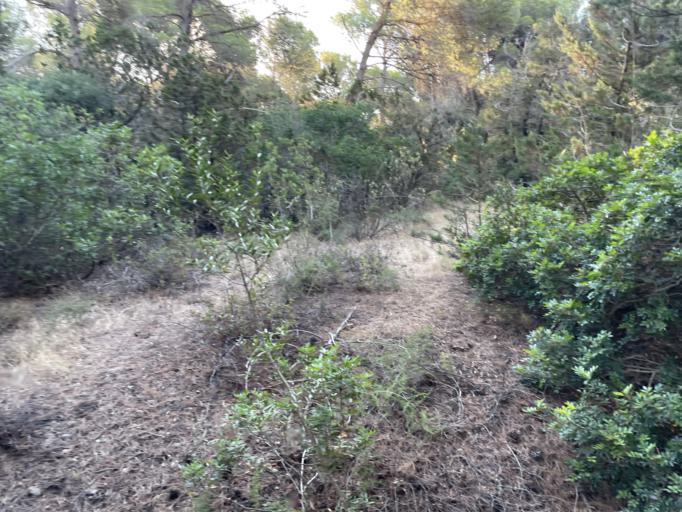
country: ES
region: Balearic Islands
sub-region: Illes Balears
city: Capdepera
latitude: 39.7153
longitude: 3.4534
